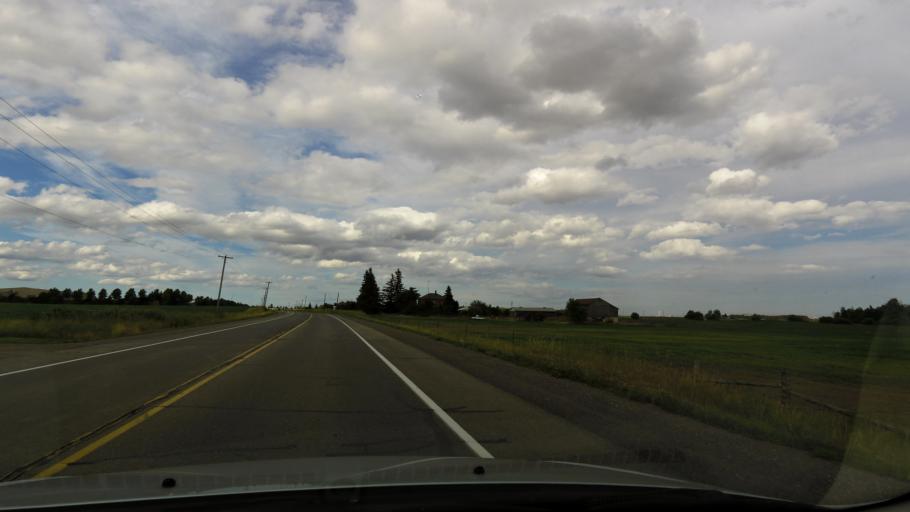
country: CA
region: Ontario
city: Brampton
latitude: 43.6874
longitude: -79.8741
